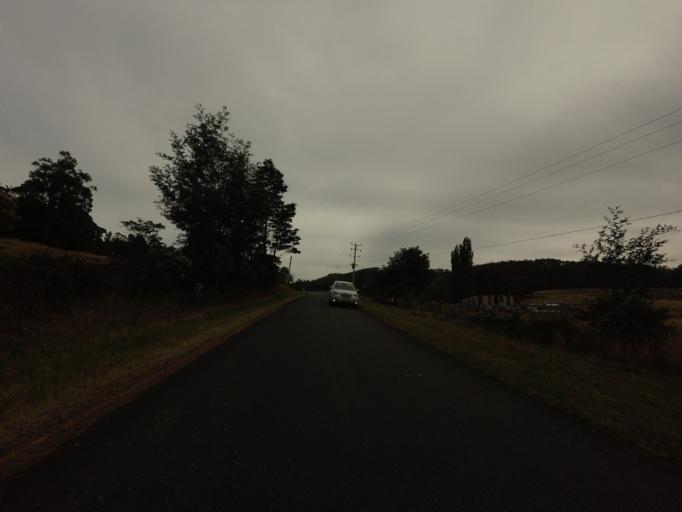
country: AU
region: Tasmania
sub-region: Sorell
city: Sorell
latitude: -42.5277
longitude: 147.5625
